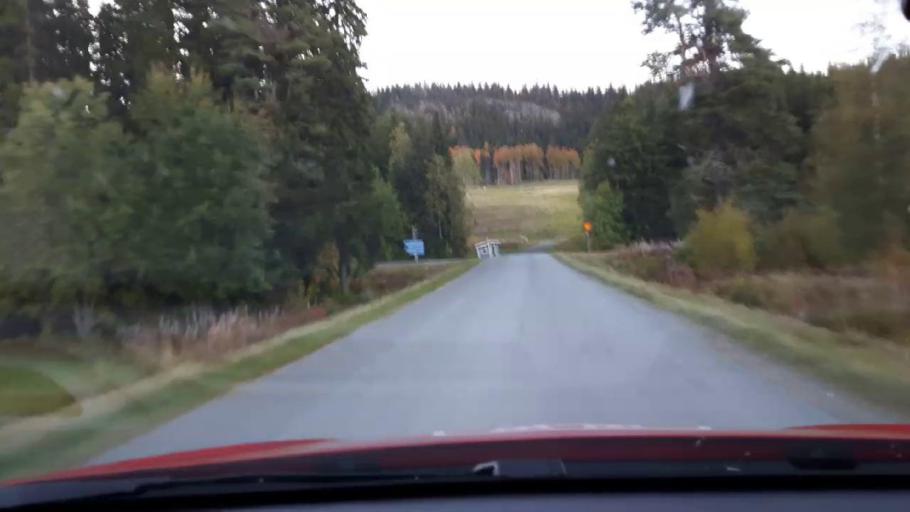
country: SE
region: Jaemtland
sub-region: Krokoms Kommun
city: Krokom
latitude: 63.4869
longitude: 14.2014
